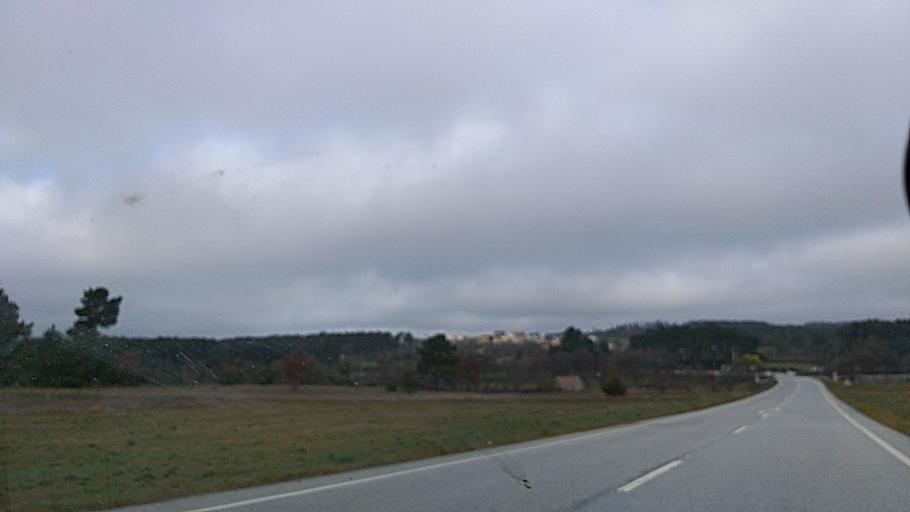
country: PT
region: Guarda
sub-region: Fornos de Algodres
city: Fornos de Algodres
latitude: 40.7159
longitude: -7.4873
